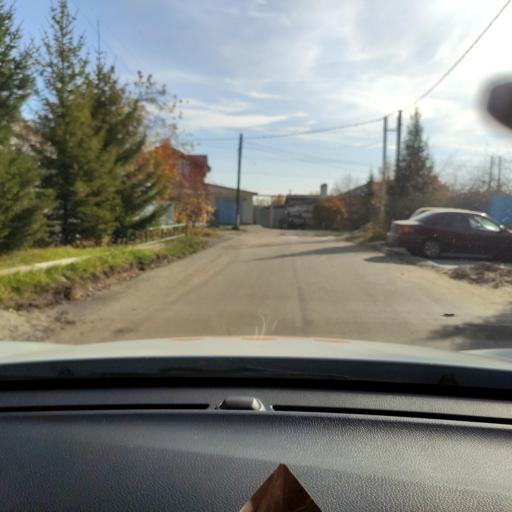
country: RU
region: Tatarstan
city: Vysokaya Gora
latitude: 55.8050
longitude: 49.2696
